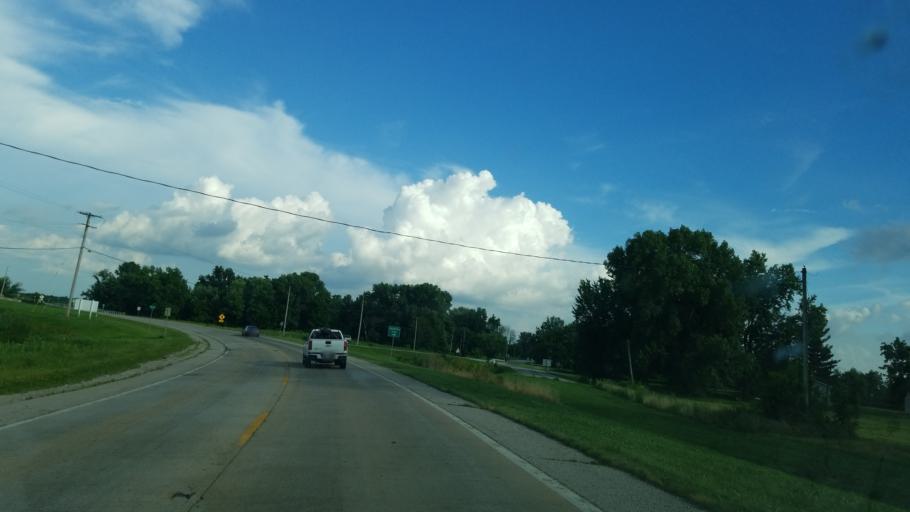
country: US
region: Illinois
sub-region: Marion County
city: Sandoval
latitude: 38.6067
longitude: -89.1153
